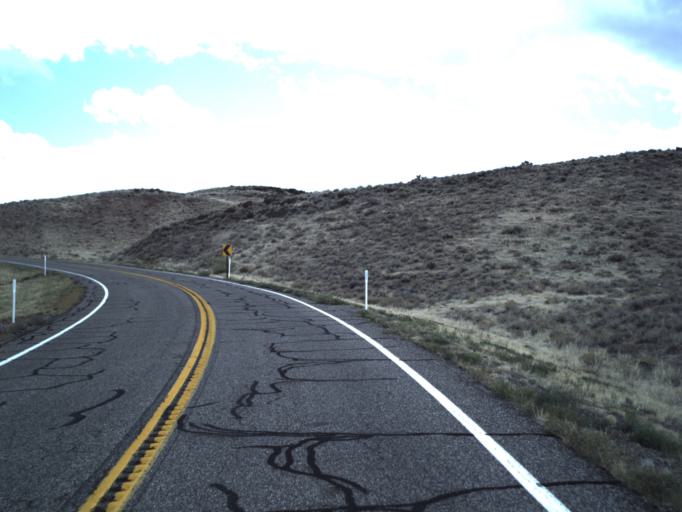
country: US
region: Utah
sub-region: Sevier County
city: Monroe
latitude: 38.6313
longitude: -112.1853
